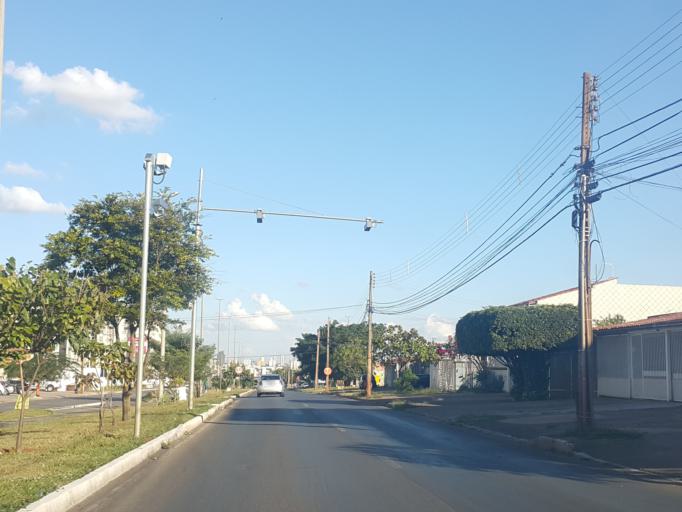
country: BR
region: Federal District
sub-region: Brasilia
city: Brasilia
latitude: -15.8315
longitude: -48.0910
